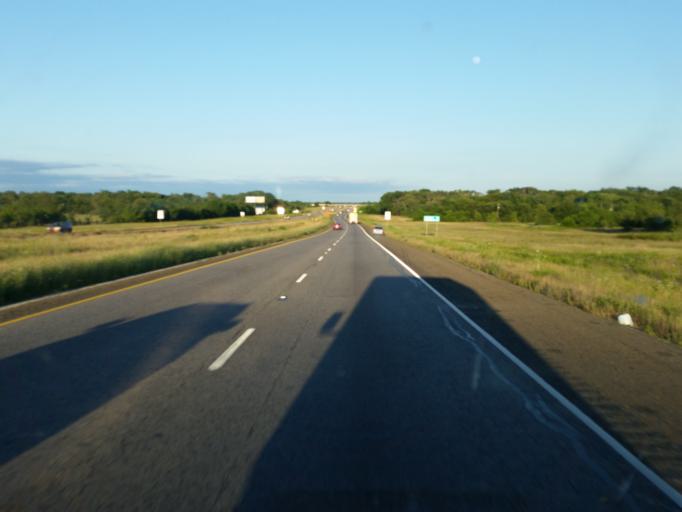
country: US
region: Texas
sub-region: Van Zandt County
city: Wills Point
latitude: 32.6521
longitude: -96.0816
